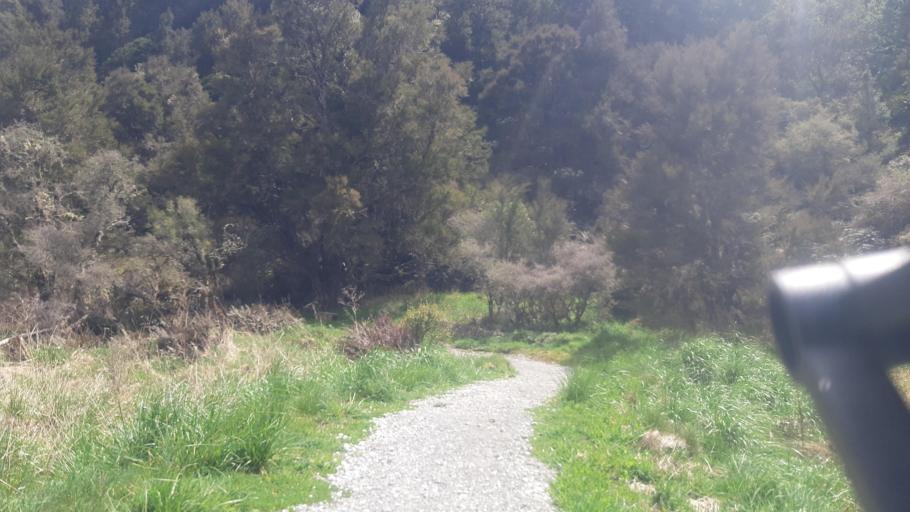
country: NZ
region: Tasman
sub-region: Tasman District
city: Wakefield
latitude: -41.7926
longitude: 172.8331
